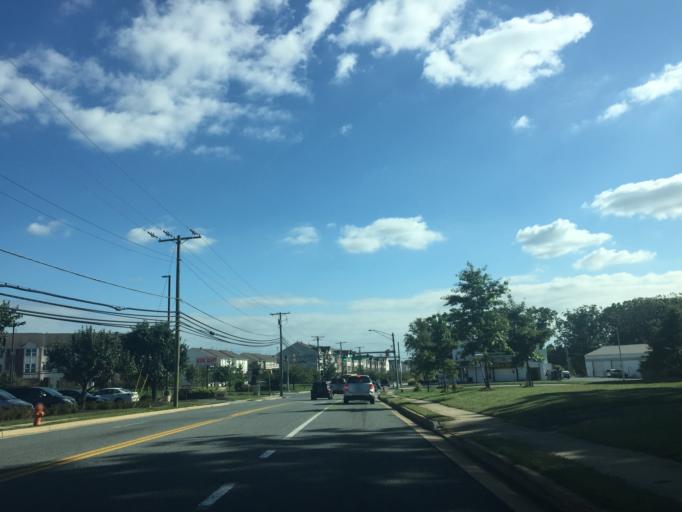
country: US
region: Maryland
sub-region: Baltimore County
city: Middle River
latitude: 39.3491
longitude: -76.4508
